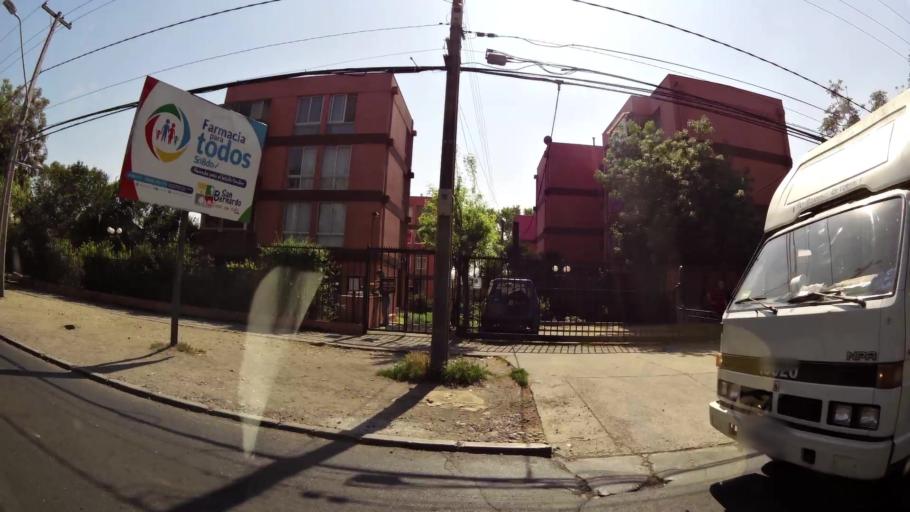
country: CL
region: Santiago Metropolitan
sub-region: Provincia de Maipo
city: San Bernardo
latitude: -33.5889
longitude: -70.7071
